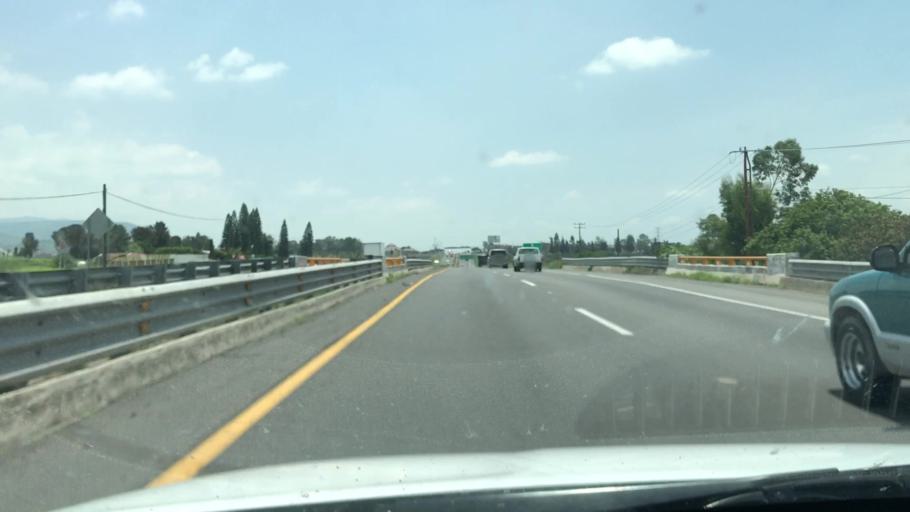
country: MX
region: Guanajuato
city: Penjamo
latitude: 20.4102
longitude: -101.7361
